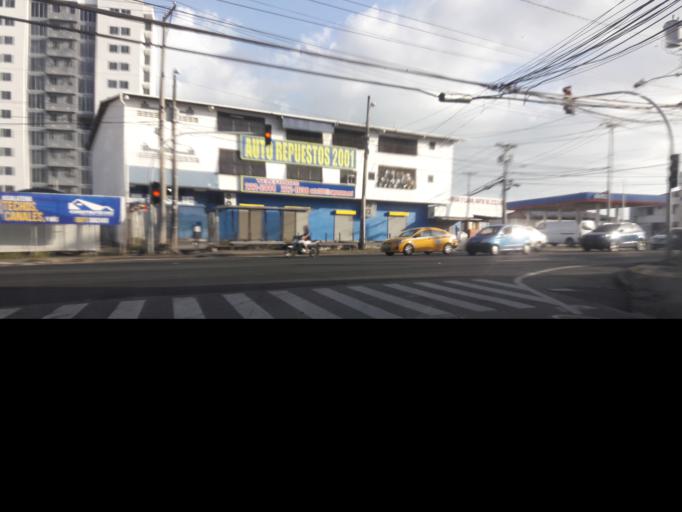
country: PA
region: Panama
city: San Miguelito
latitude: 9.0198
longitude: -79.4919
